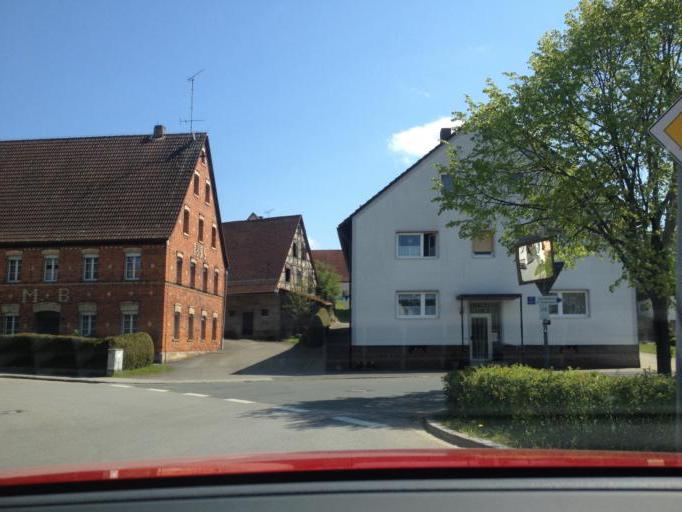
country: DE
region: Bavaria
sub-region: Regierungsbezirk Mittelfranken
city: Schnaittach
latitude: 49.5696
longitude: 11.3414
